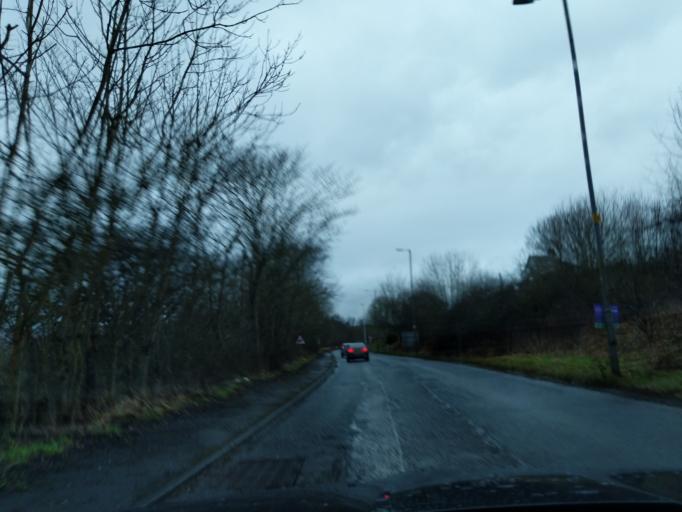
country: GB
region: Scotland
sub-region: The Scottish Borders
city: Galashiels
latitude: 55.6289
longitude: -2.8292
